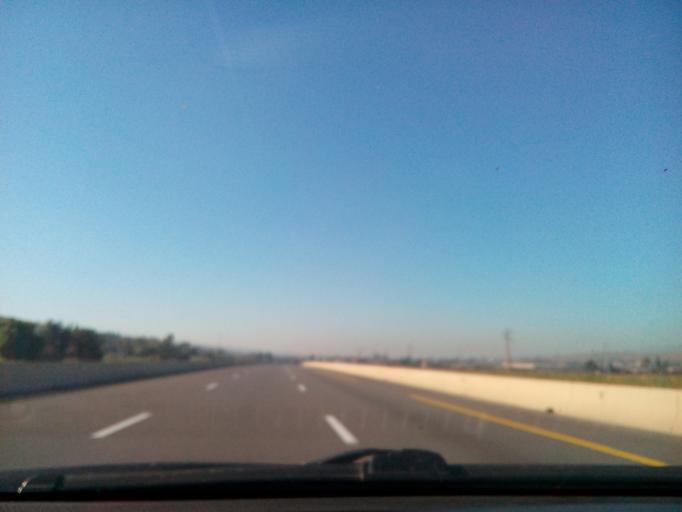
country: DZ
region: Chlef
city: Boukadir
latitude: 36.0368
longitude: 1.0845
